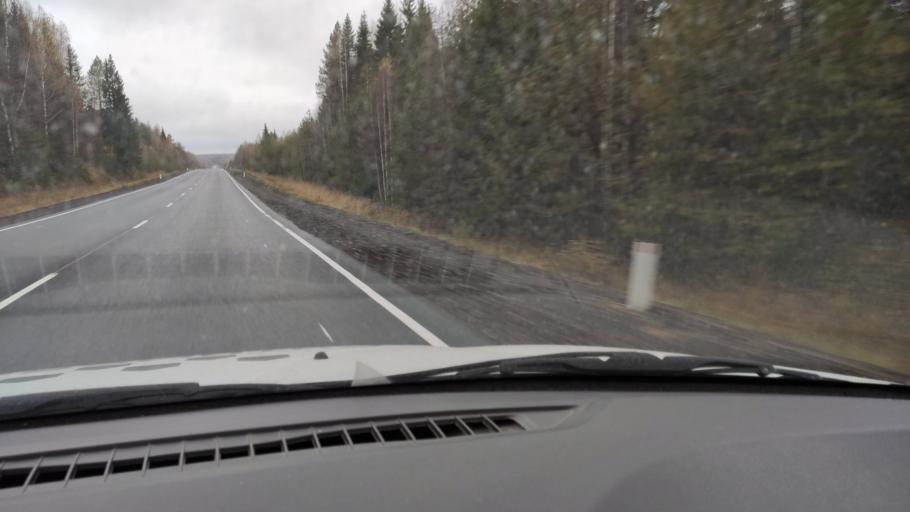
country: RU
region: Kirov
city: Chernaya Kholunitsa
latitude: 58.8869
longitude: 51.3863
